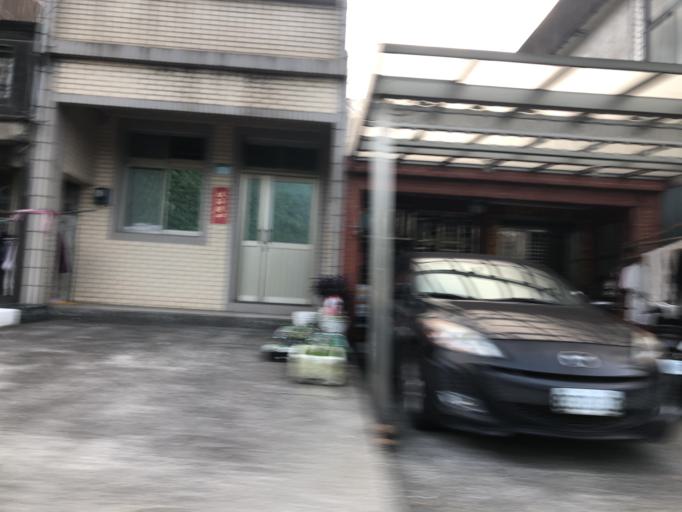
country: TW
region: Taiwan
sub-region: Keelung
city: Keelung
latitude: 25.2025
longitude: 121.6465
